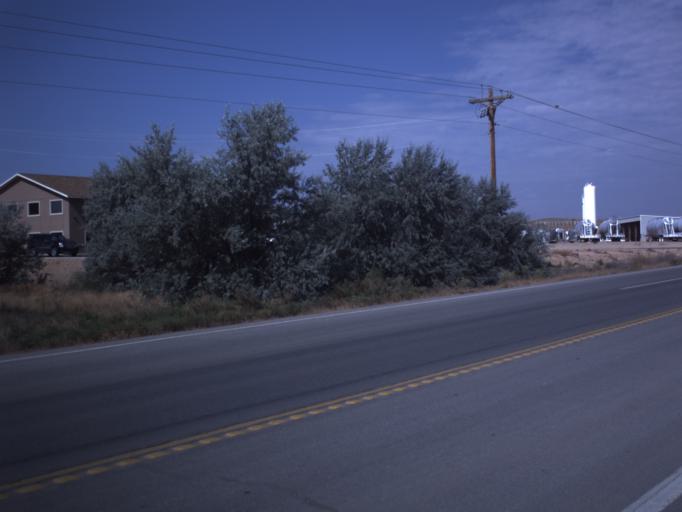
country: US
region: Utah
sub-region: Uintah County
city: Naples
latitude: 40.3830
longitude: -109.4264
